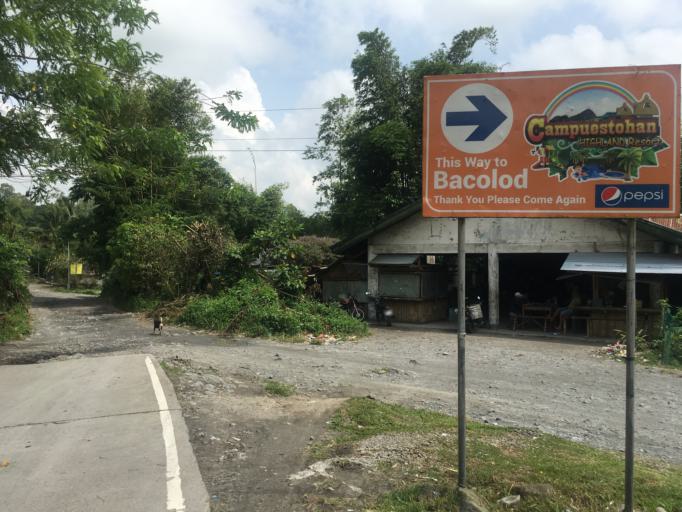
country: PH
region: Western Visayas
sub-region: Province of Negros Occidental
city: Alegria
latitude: 10.6615
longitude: 123.1125
